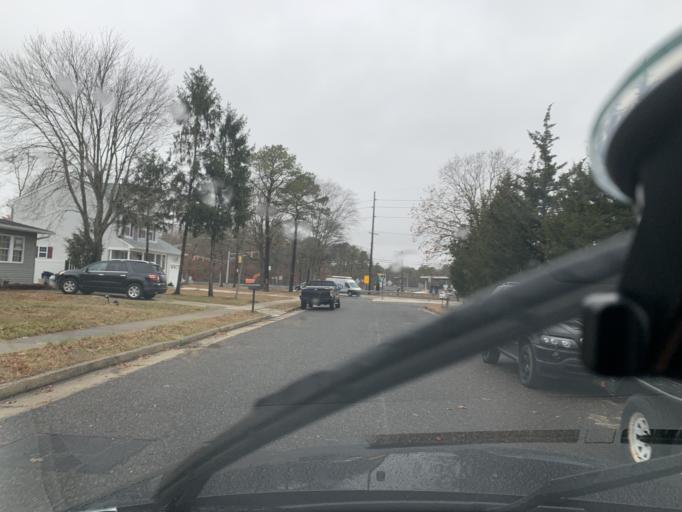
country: US
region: New Jersey
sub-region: Atlantic County
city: Pomona
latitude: 39.4341
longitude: -74.5907
